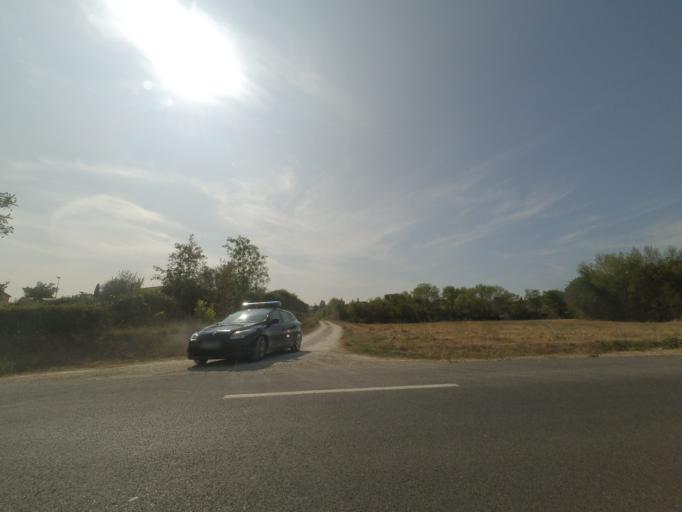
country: FR
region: Languedoc-Roussillon
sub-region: Departement du Gard
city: Saint-Mamert-du-Gard
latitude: 43.8867
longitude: 4.1943
